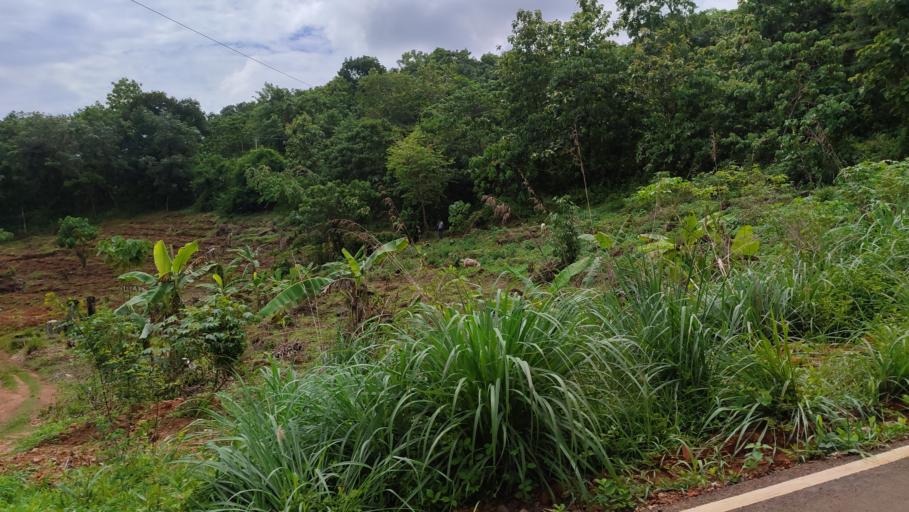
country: IN
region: Kerala
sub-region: Kasaragod District
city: Nileshwar
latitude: 12.2840
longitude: 75.2610
